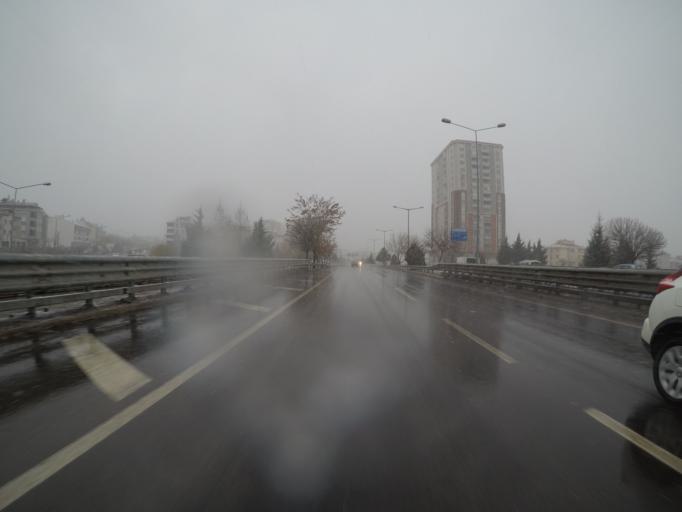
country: TR
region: Nevsehir
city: Nevsehir
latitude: 38.6307
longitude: 34.7293
